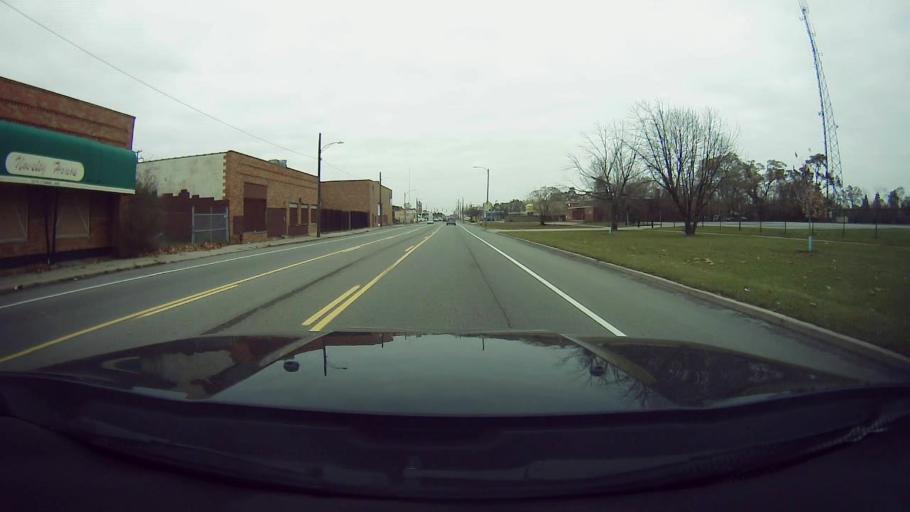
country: US
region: Michigan
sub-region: Wayne County
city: Hamtramck
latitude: 42.4138
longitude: -83.0602
